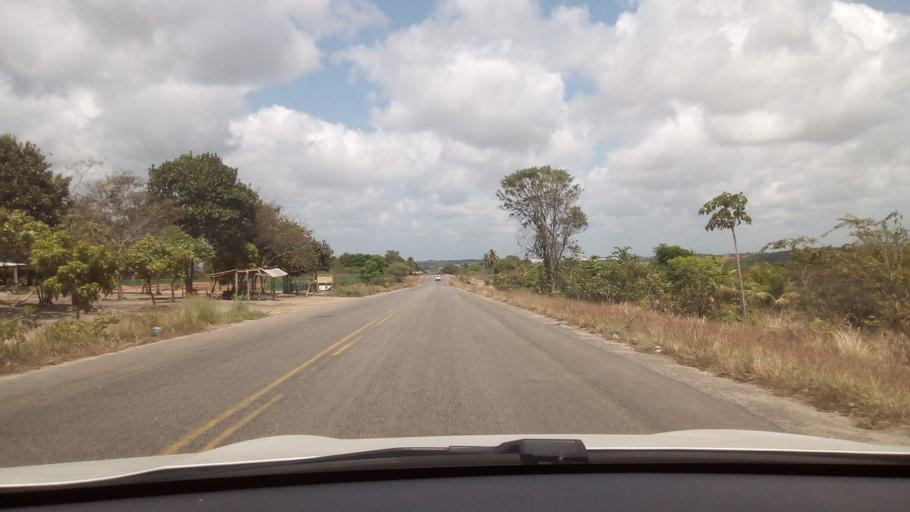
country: BR
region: Paraiba
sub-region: Conde
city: Conde
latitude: -7.2451
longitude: -34.8308
